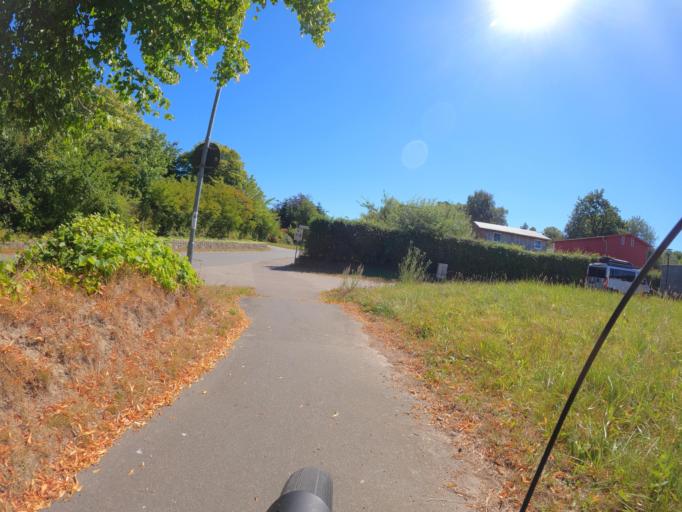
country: DE
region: Schleswig-Holstein
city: Quern
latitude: 54.7833
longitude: 9.7260
